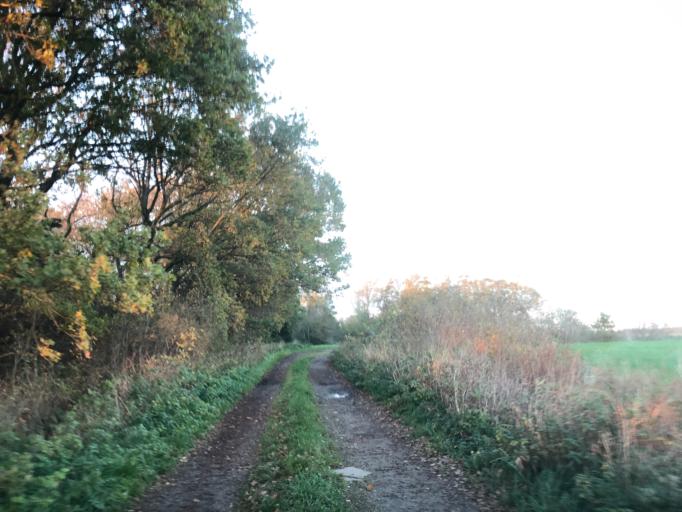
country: DK
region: Central Jutland
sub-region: Holstebro Kommune
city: Ulfborg
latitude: 56.2906
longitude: 8.2924
